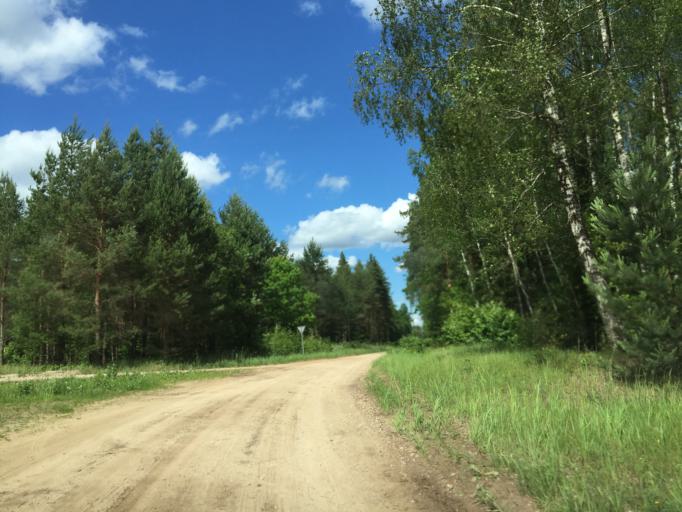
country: LV
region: Lecava
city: Iecava
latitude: 56.5617
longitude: 24.3121
